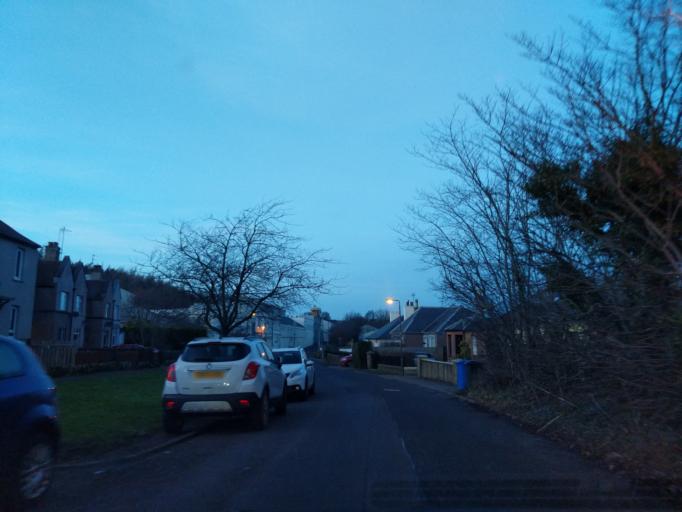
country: GB
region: Scotland
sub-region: Midlothian
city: Loanhead
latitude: 55.8796
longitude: -3.1423
